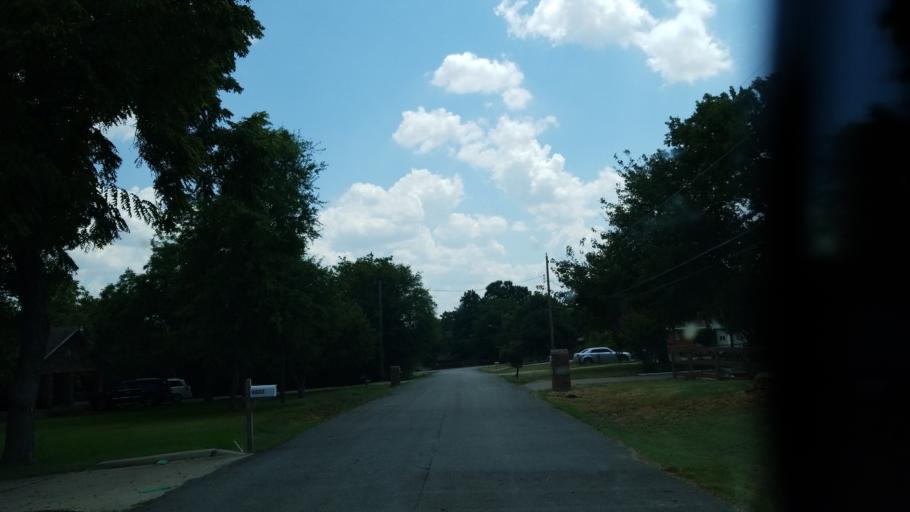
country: US
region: Texas
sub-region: Dallas County
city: Duncanville
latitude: 32.6738
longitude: -96.8892
